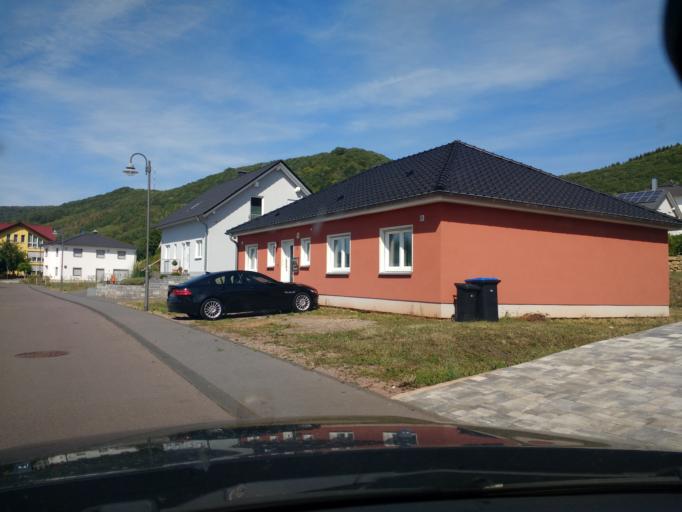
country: DE
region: Rheinland-Pfalz
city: Irsch
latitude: 49.6063
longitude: 6.6006
